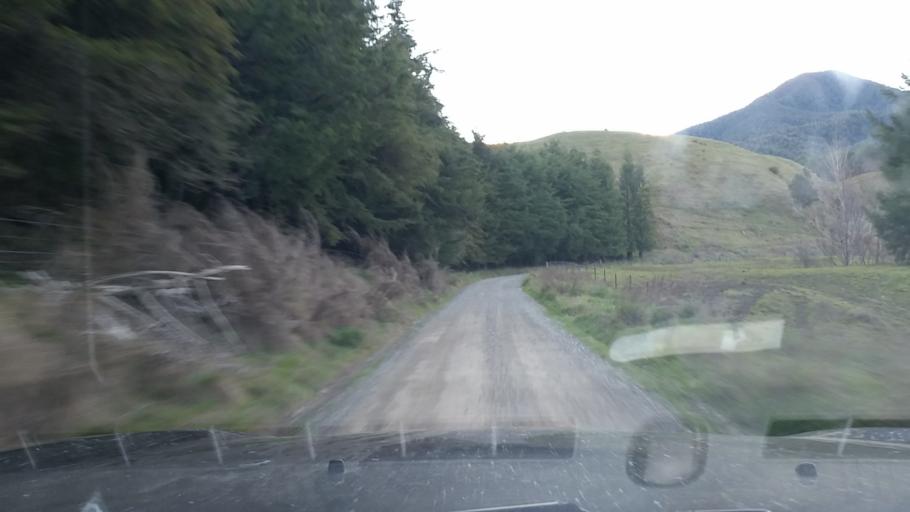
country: NZ
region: Marlborough
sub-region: Marlborough District
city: Blenheim
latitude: -41.5058
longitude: 173.5914
